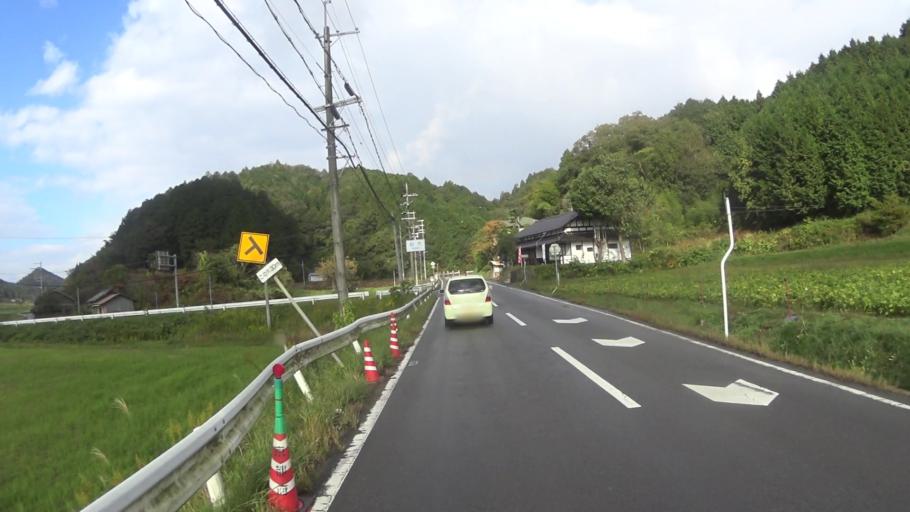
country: JP
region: Kyoto
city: Ayabe
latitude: 35.3690
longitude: 135.1929
